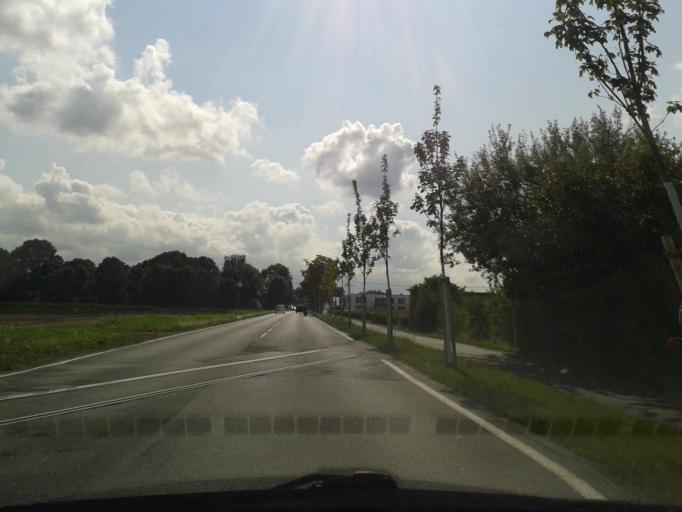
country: DE
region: North Rhine-Westphalia
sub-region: Regierungsbezirk Detmold
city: Paderborn
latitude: 51.7021
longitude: 8.7169
